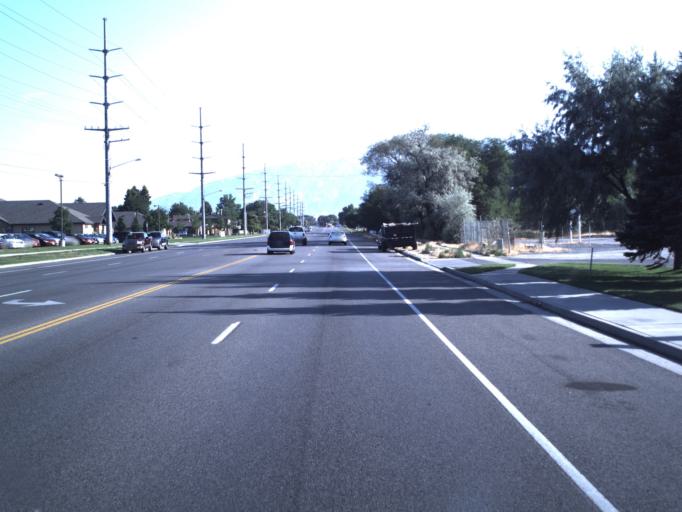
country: US
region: Utah
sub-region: Utah County
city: American Fork
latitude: 40.3647
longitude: -111.7854
